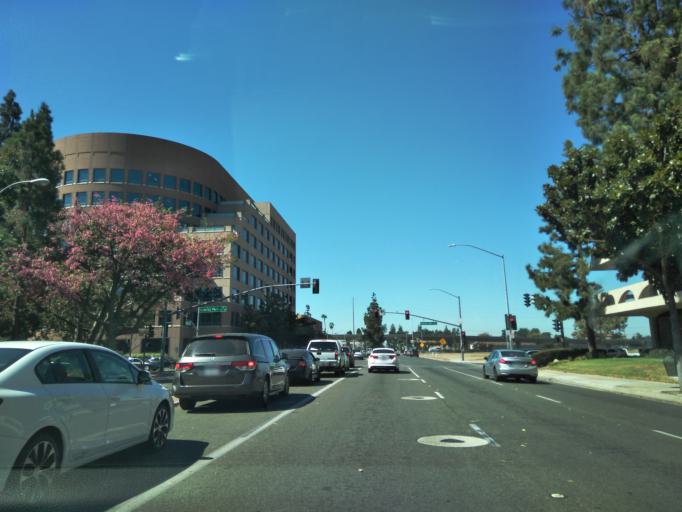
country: US
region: California
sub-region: Orange County
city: Tustin
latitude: 33.7482
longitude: -117.8400
